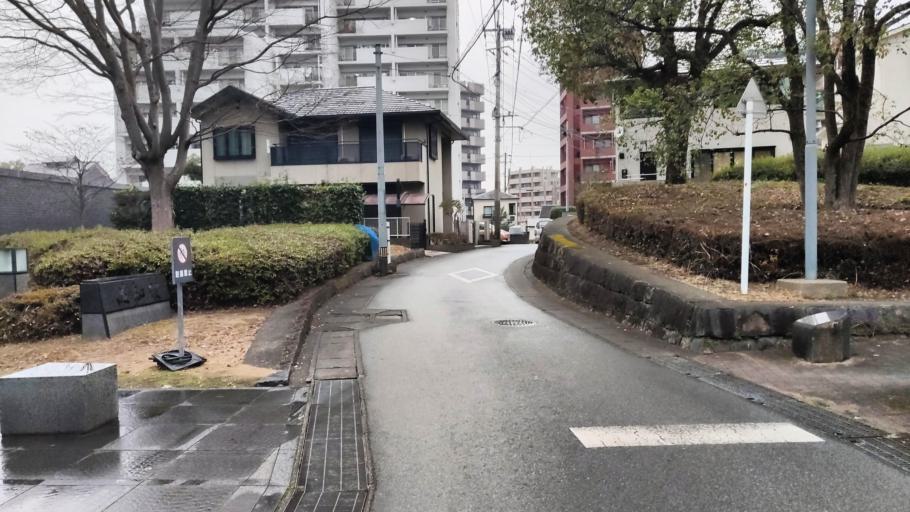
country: JP
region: Kumamoto
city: Kumamoto
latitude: 32.7862
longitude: 130.7357
